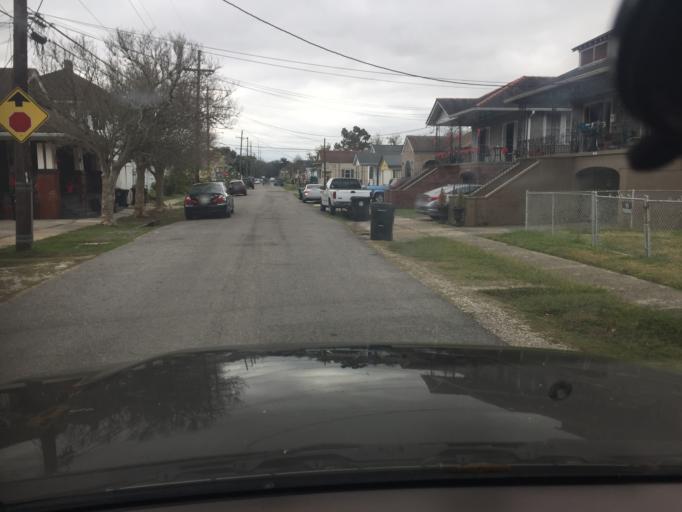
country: US
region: Louisiana
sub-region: Orleans Parish
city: New Orleans
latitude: 29.9842
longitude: -90.0750
